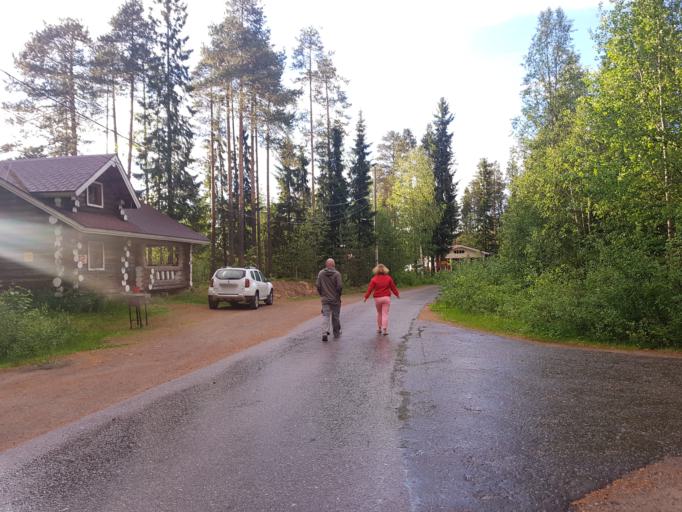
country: RU
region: Republic of Karelia
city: Kostomuksha
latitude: 64.6009
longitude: 30.5744
